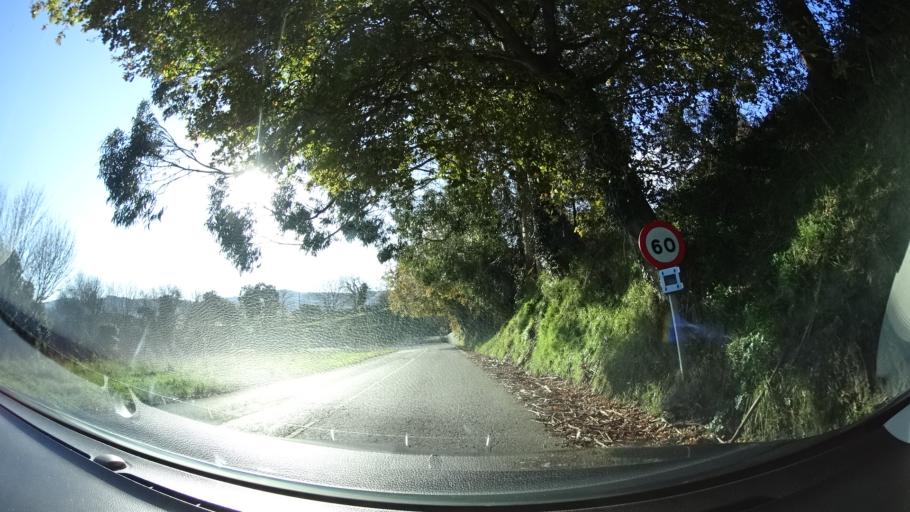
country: ES
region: Basque Country
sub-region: Bizkaia
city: Bermeo
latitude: 43.4267
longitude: -2.7414
